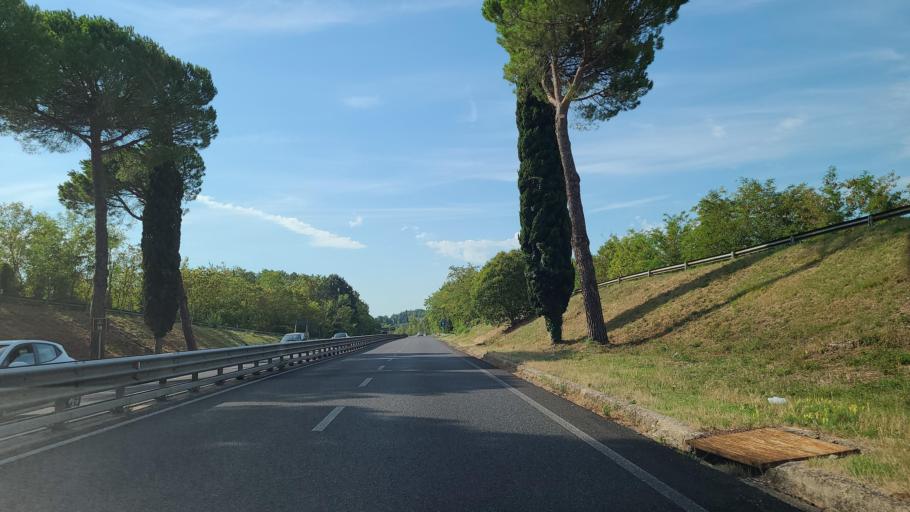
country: IT
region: Tuscany
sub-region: Province of Florence
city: Sambuca
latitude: 43.5521
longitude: 11.2102
